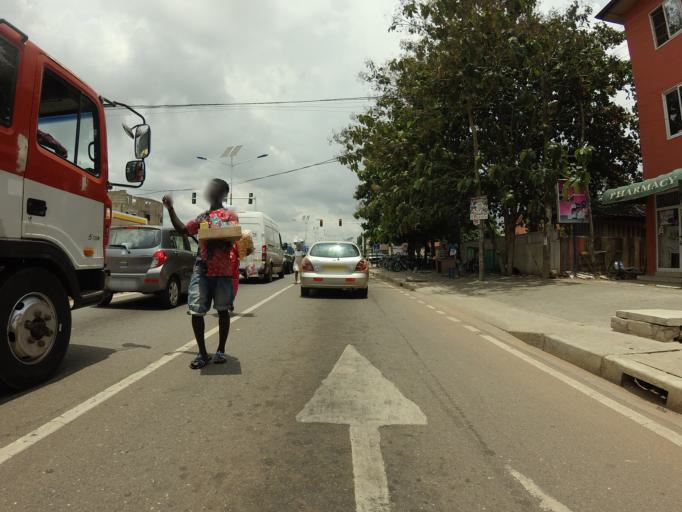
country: GH
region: Greater Accra
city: Medina Estates
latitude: 5.6502
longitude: -0.1505
